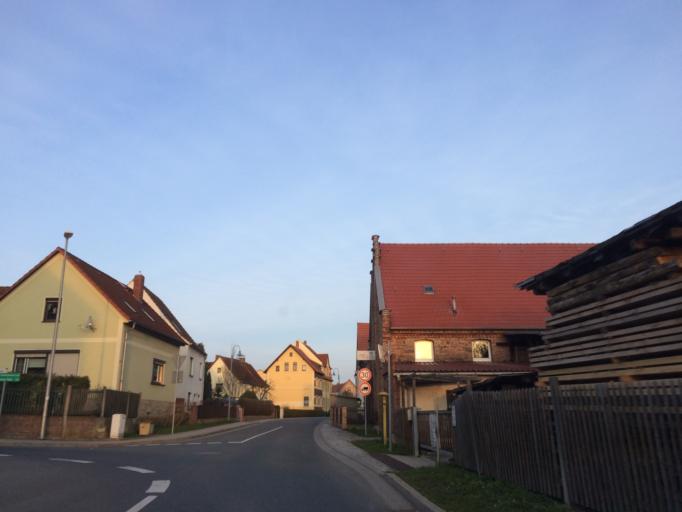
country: DE
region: Thuringia
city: Eisenberg
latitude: 50.9704
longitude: 11.8815
